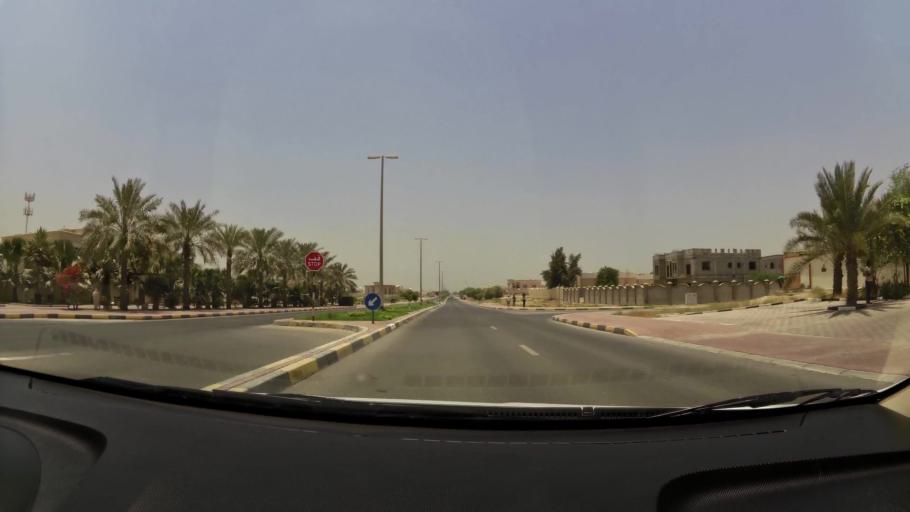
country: AE
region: Ajman
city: Ajman
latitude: 25.4065
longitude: 55.4912
